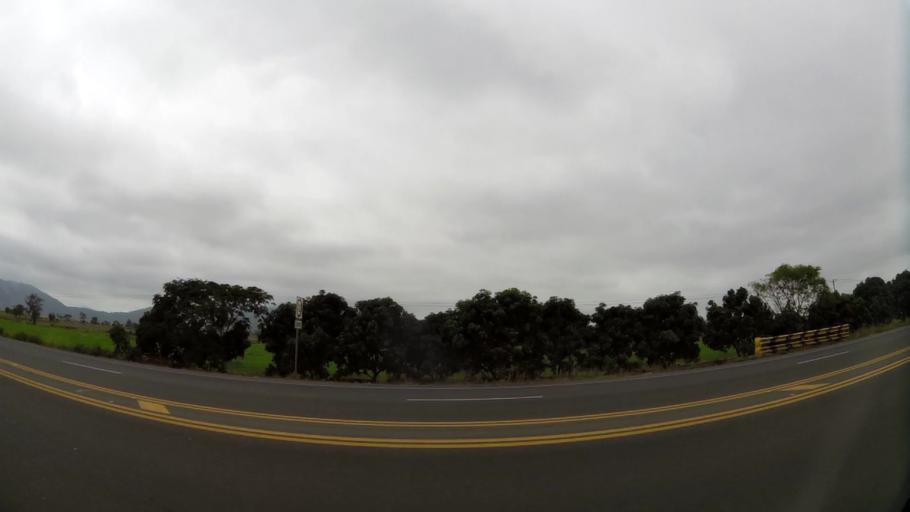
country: EC
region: Guayas
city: Naranjal
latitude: -2.4966
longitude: -79.5999
